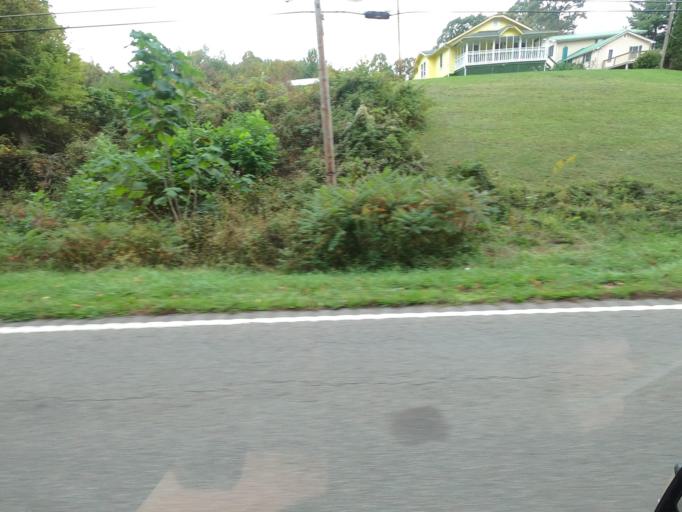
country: US
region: Tennessee
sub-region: Carter County
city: Elizabethton
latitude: 36.2606
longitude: -82.2229
